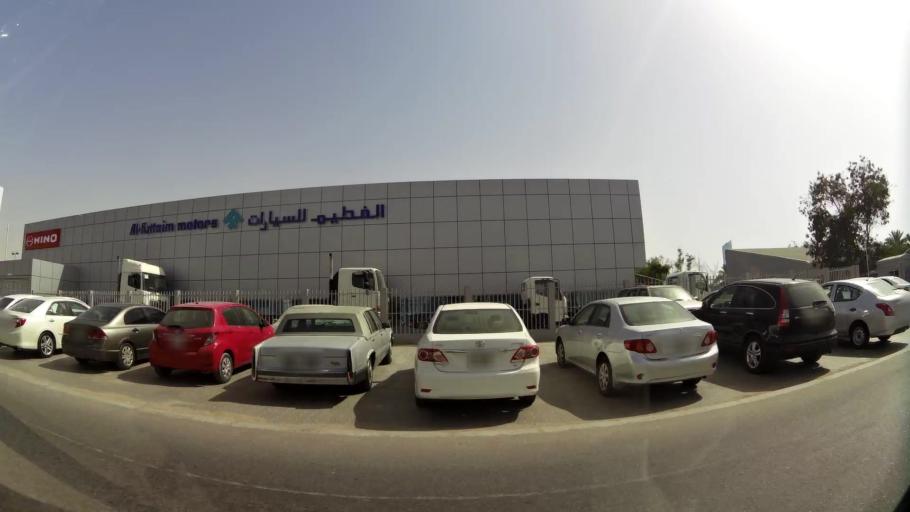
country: AE
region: Ash Shariqah
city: Sharjah
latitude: 25.2352
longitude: 55.3621
